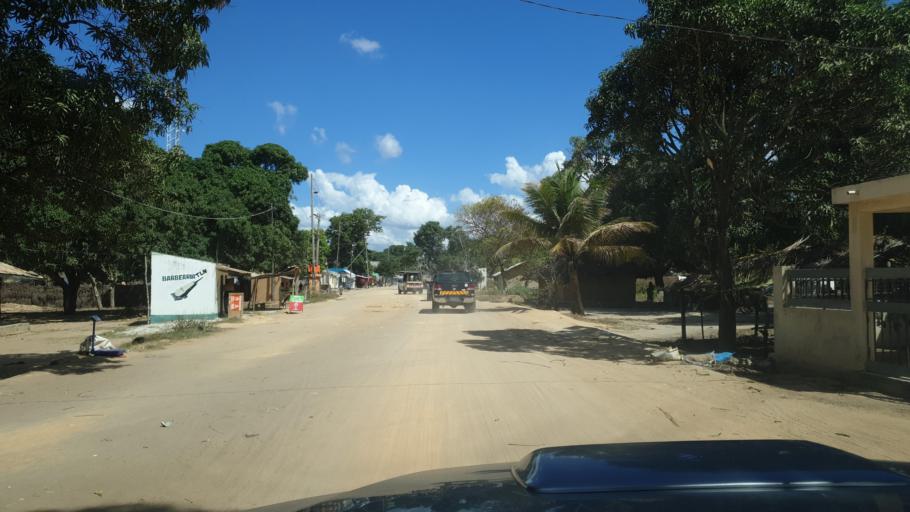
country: MZ
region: Nampula
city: Nacala
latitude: -14.5715
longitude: 40.6932
